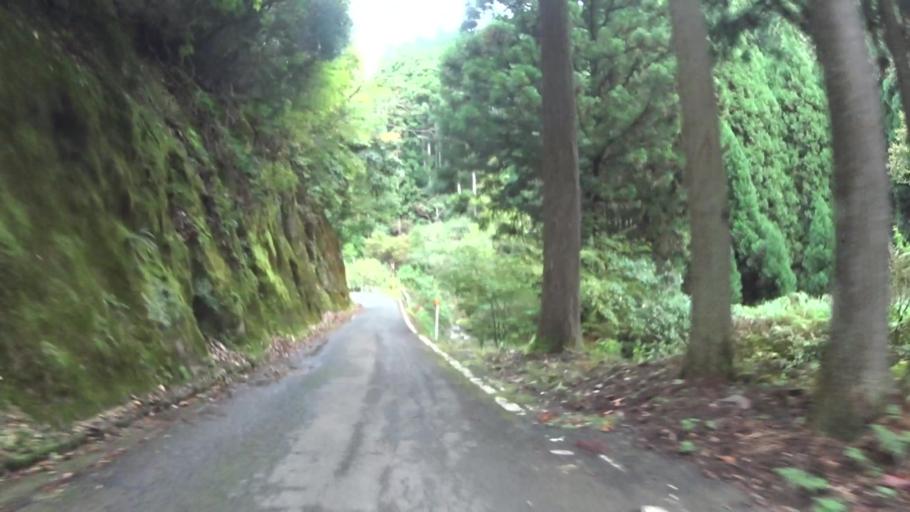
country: JP
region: Fukui
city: Obama
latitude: 35.2784
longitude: 135.6972
